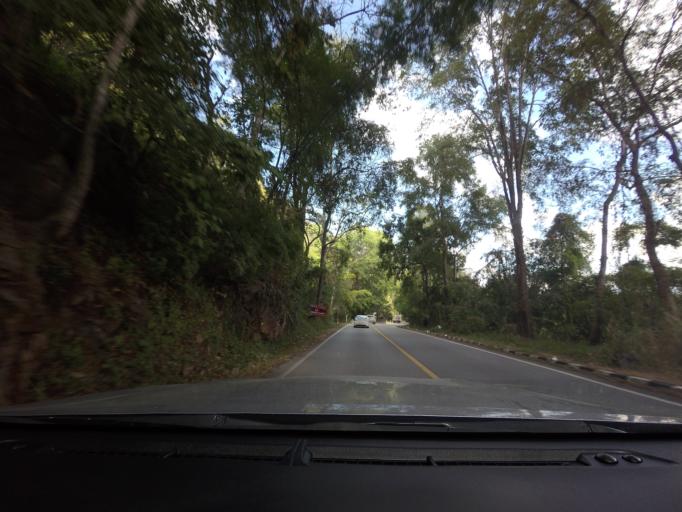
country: TH
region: Chiang Mai
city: Chai Prakan
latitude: 19.6037
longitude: 99.1197
